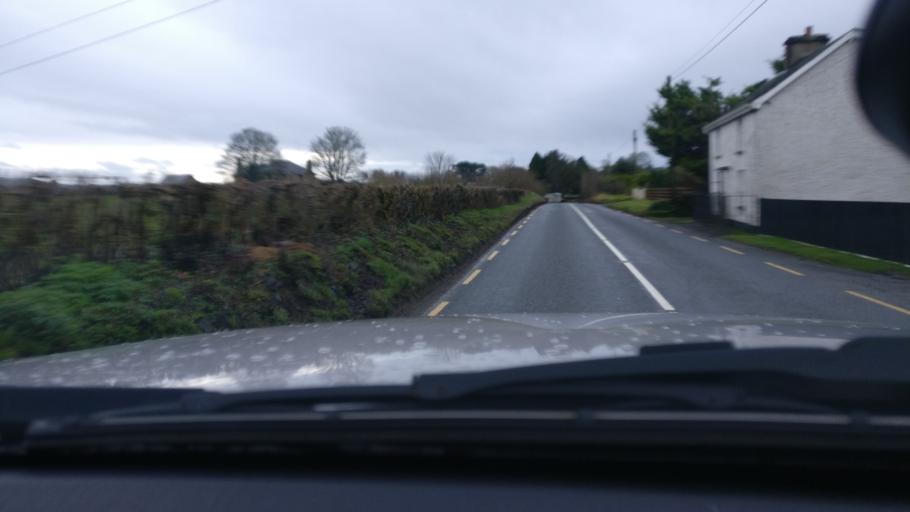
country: IE
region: Leinster
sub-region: An Longfort
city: Granard
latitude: 53.8087
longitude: -7.3759
